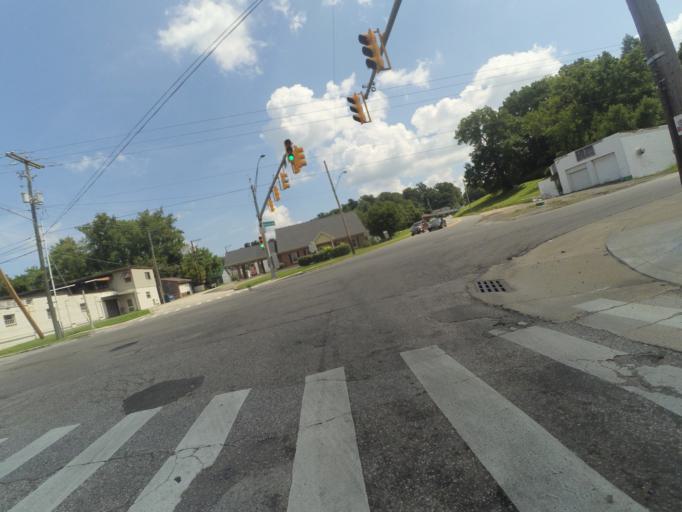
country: US
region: West Virginia
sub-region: Cabell County
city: Huntington
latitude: 38.4138
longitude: -82.4201
